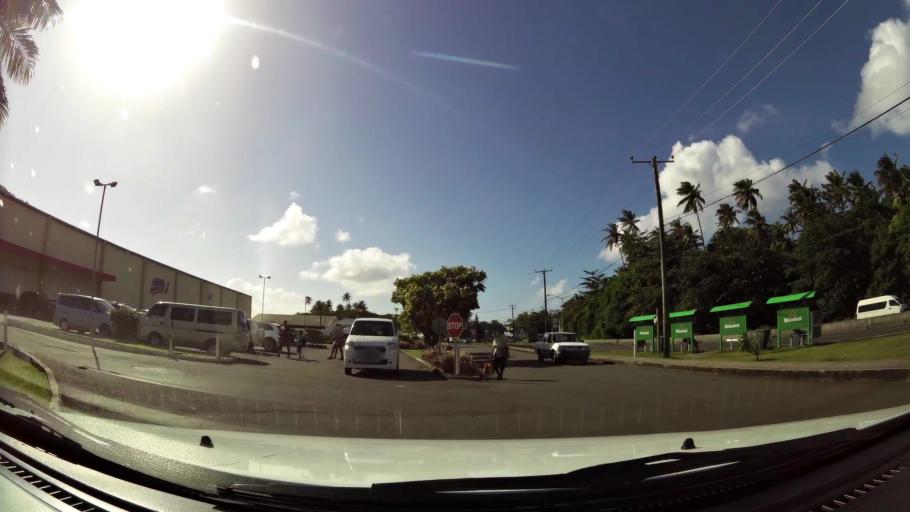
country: LC
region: Castries Quarter
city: Bisee
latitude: 14.0344
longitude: -60.9703
